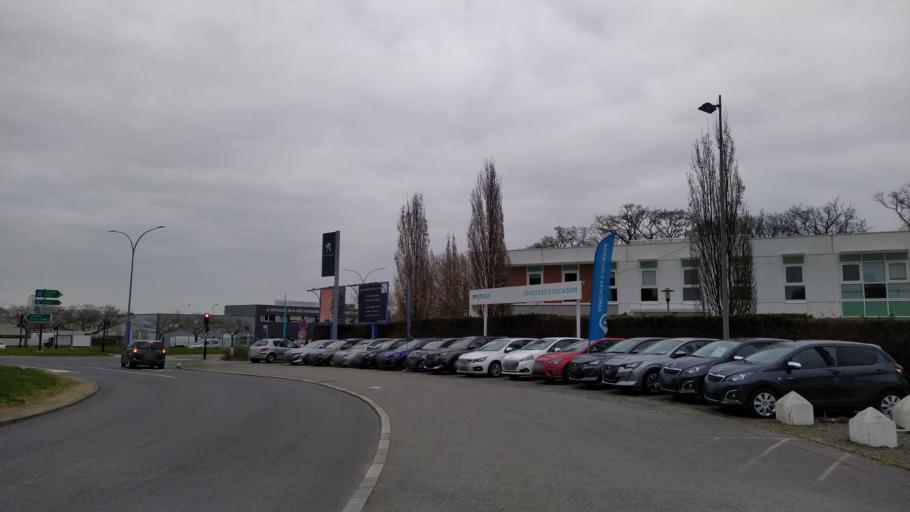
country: FR
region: Pays de la Loire
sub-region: Departement de la Loire-Atlantique
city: Sainte-Luce-sur-Loire
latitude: 47.2599
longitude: -1.4990
